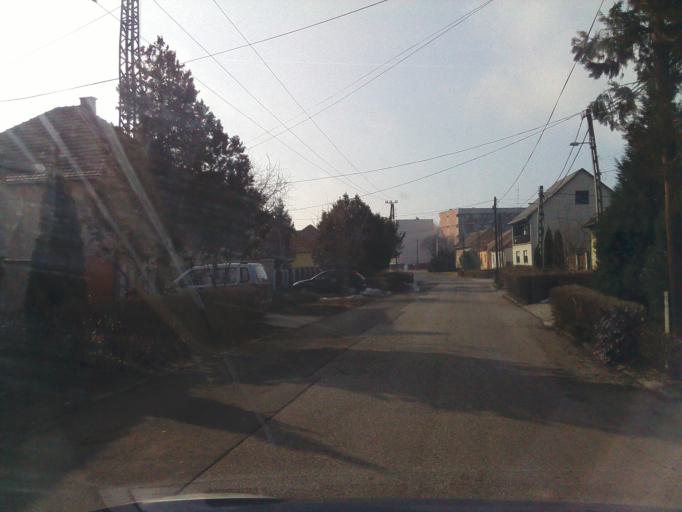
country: HU
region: Heves
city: Hatvan
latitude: 47.6695
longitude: 19.6971
